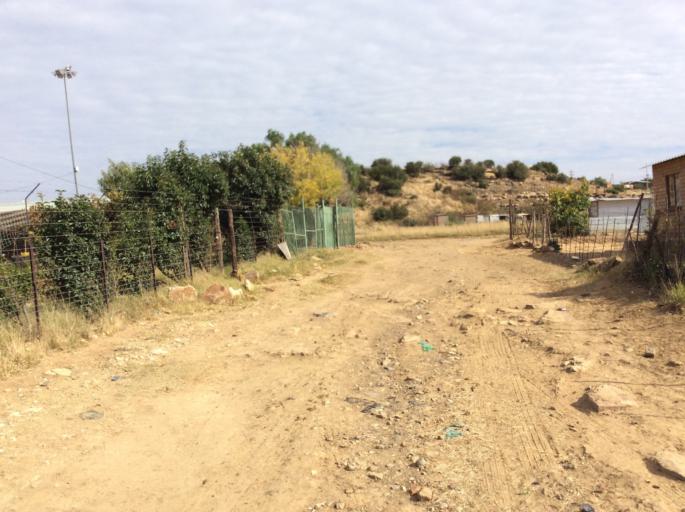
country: LS
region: Mafeteng
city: Mafeteng
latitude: -29.7204
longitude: 27.0203
